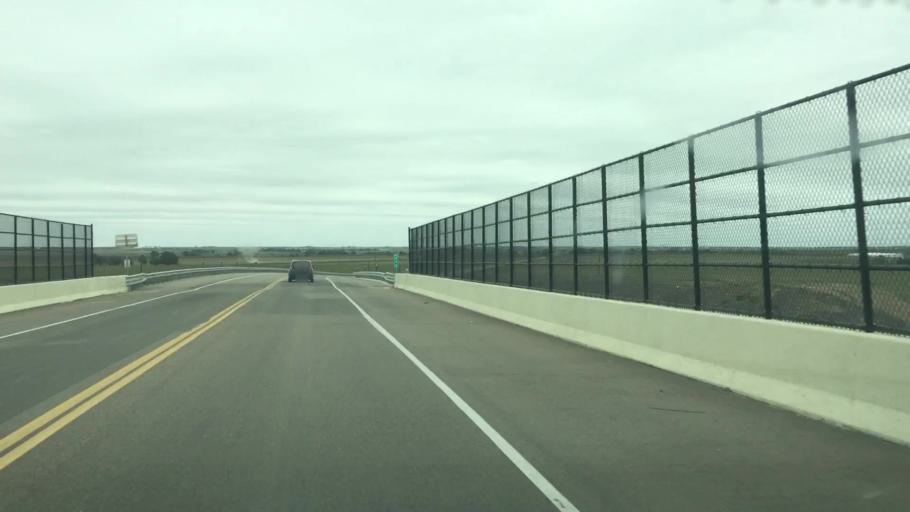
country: US
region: Colorado
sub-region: Prowers County
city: Lamar
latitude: 38.0520
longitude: -102.2555
